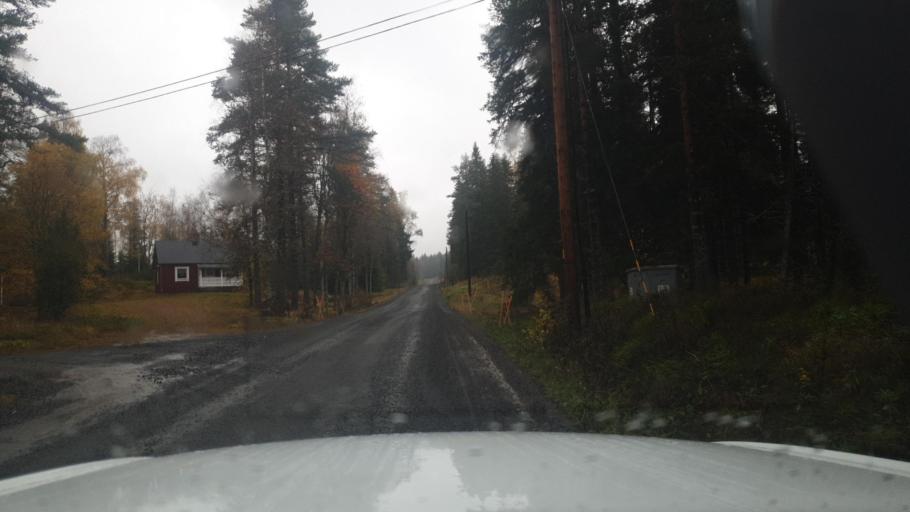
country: SE
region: Vaermland
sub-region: Eda Kommun
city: Charlottenberg
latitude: 60.1531
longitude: 12.5970
